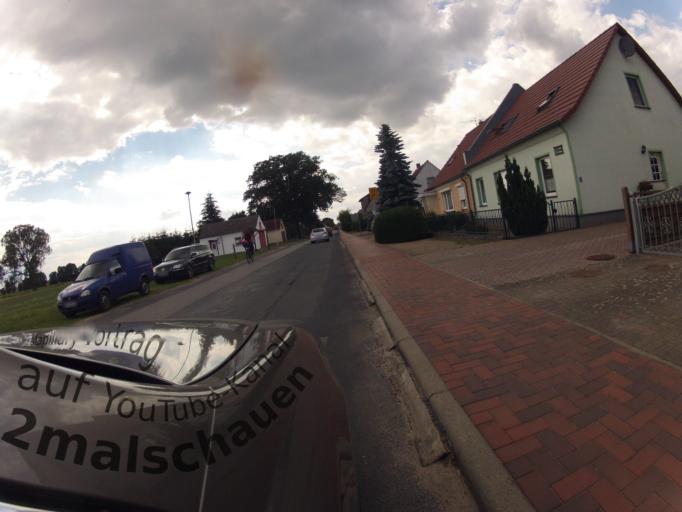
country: DE
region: Mecklenburg-Vorpommern
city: Seebad Heringsdorf
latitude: 53.9113
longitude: 14.1461
